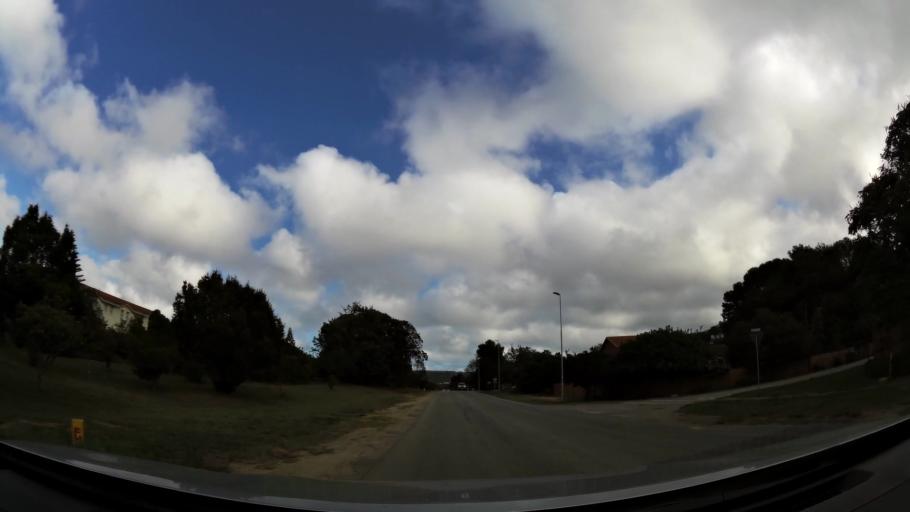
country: ZA
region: Western Cape
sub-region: Eden District Municipality
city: Plettenberg Bay
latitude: -34.0699
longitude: 23.3689
